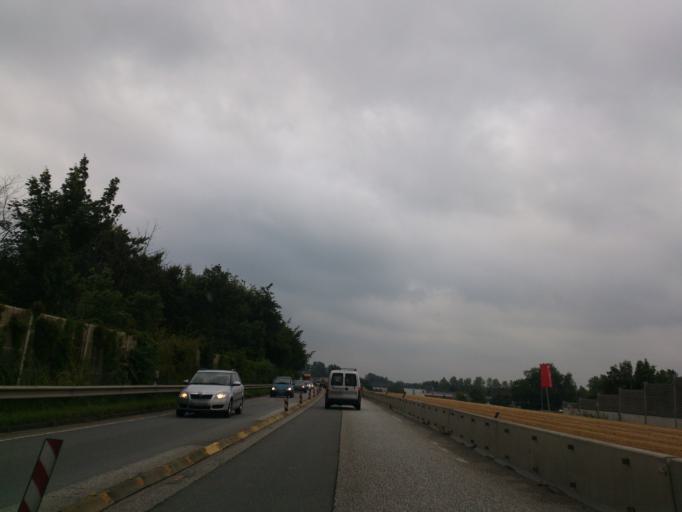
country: DE
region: Schleswig-Holstein
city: Heiligenstedtenerkamp
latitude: 53.9072
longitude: 9.4893
